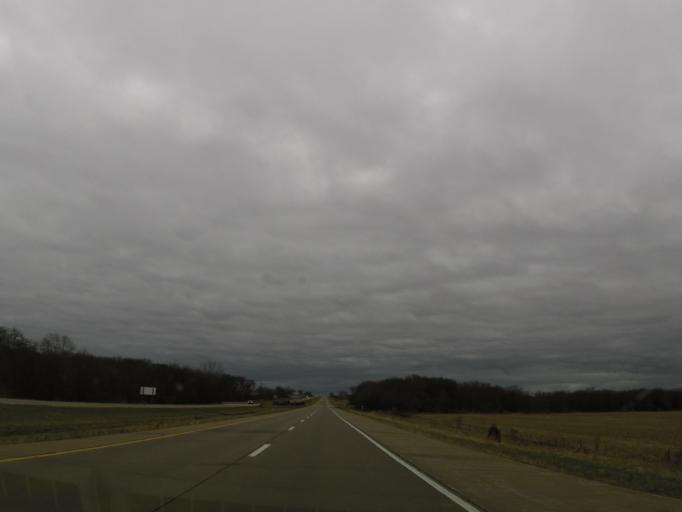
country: US
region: Iowa
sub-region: Benton County
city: Urbana
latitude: 42.3011
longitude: -91.9646
